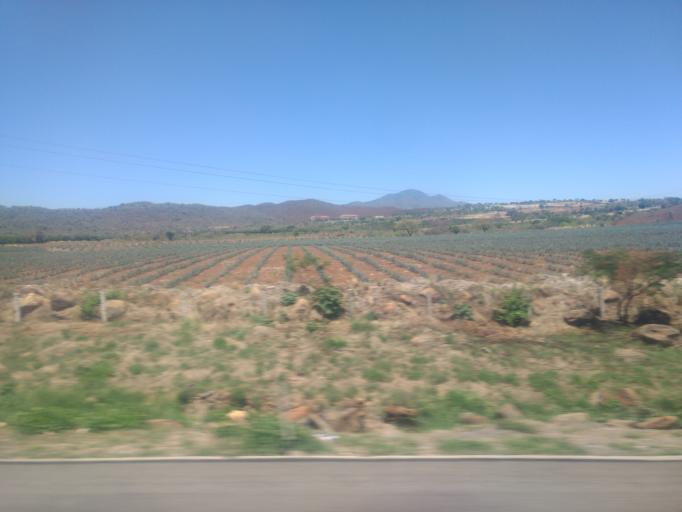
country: MX
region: Jalisco
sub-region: Acatlan de Juarez
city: Villa de los Ninos
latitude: 20.4105
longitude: -103.5587
